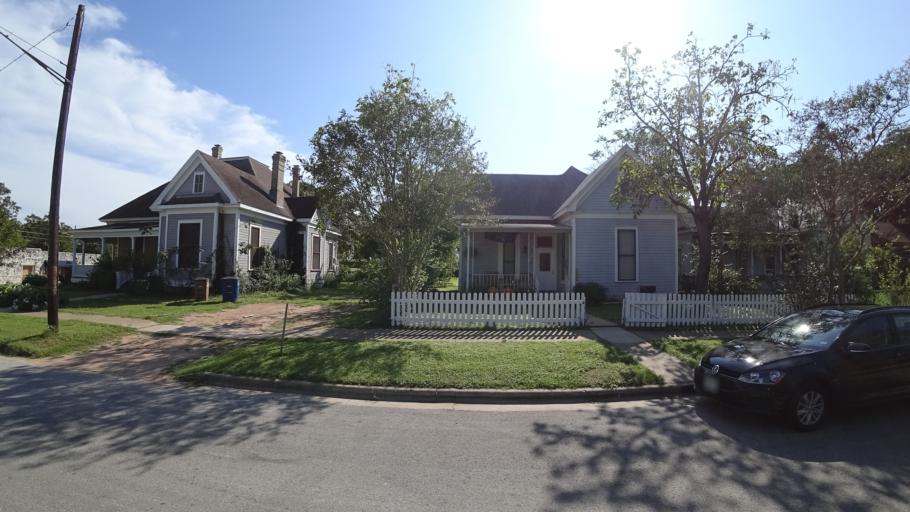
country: US
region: Texas
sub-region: Travis County
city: Austin
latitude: 30.2670
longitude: -97.7288
